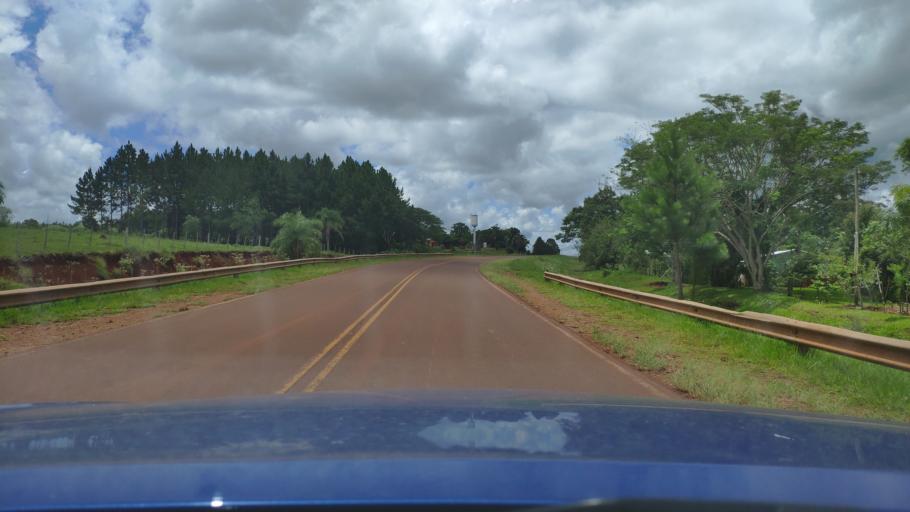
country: AR
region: Misiones
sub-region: Departamento de San Javier
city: San Javier
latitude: -27.8575
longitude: -55.2522
